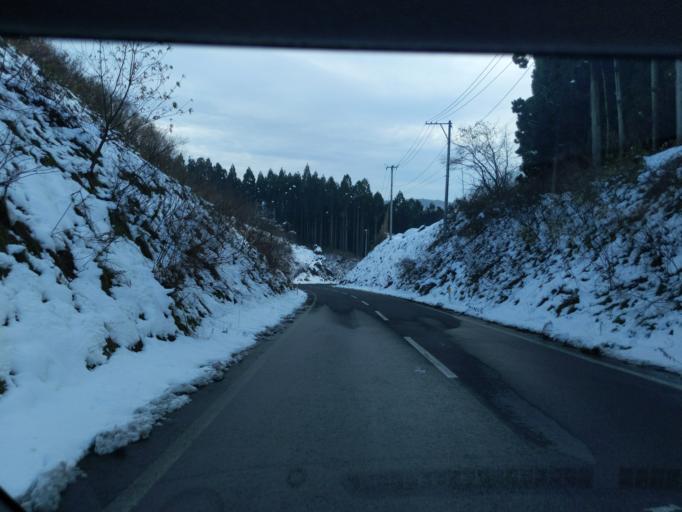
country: JP
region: Iwate
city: Mizusawa
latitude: 39.0575
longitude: 141.0864
